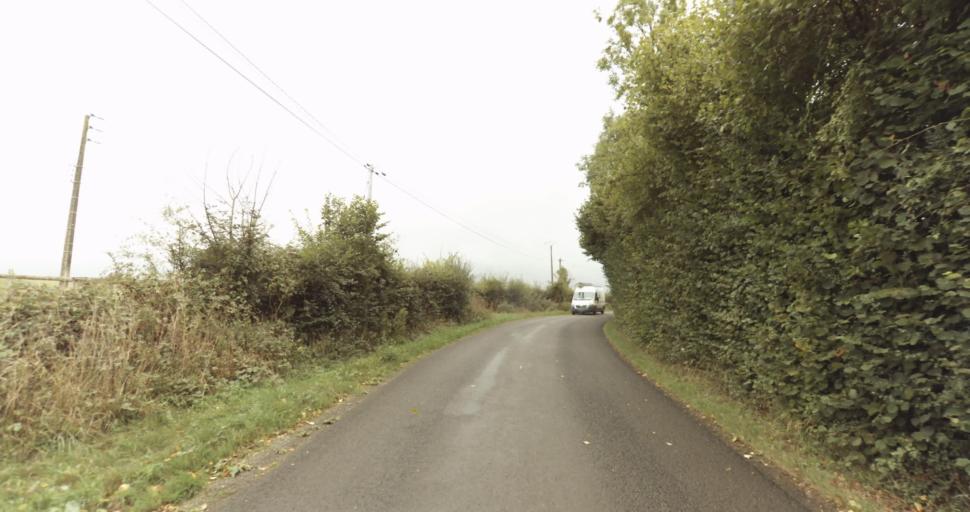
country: FR
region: Lower Normandy
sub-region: Departement de l'Orne
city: Sainte-Gauburge-Sainte-Colombe
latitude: 48.7179
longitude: 0.3797
